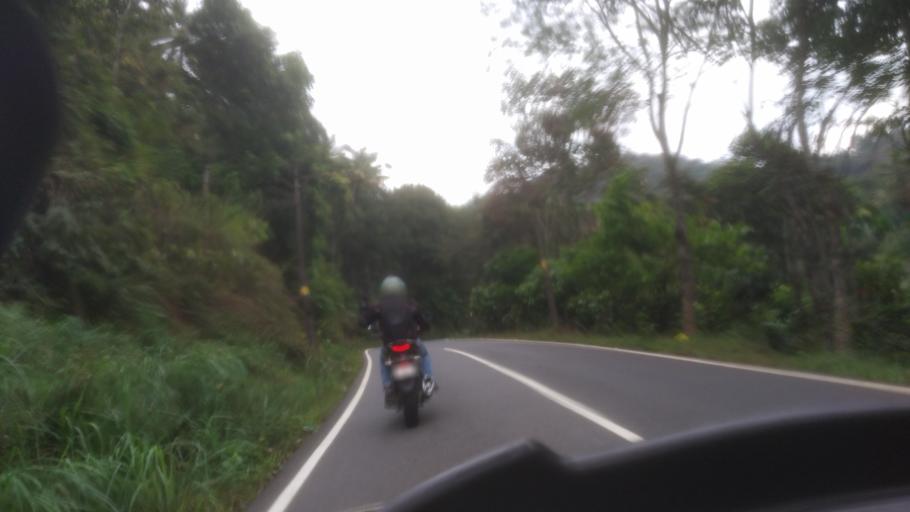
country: IN
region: Kerala
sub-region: Idukki
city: Idukki
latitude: 9.9638
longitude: 77.0006
